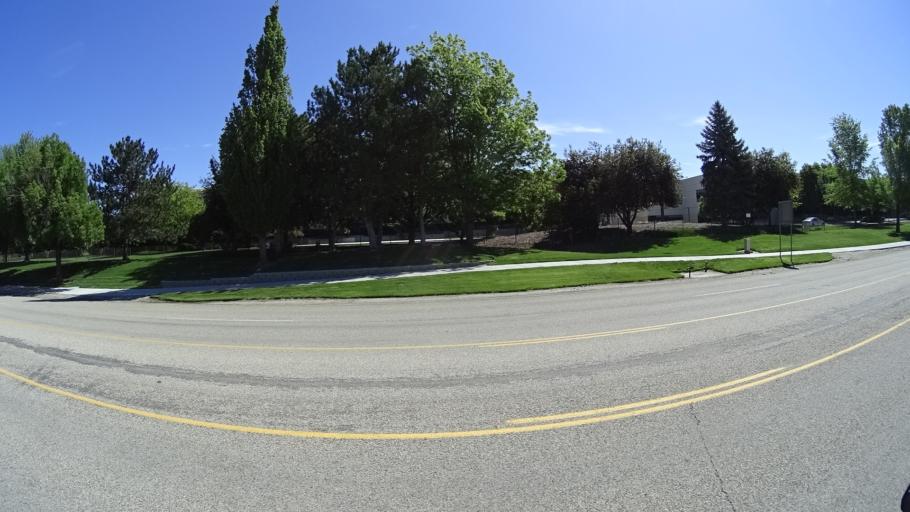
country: US
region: Idaho
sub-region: Ada County
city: Boise
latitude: 43.5275
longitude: -116.1499
